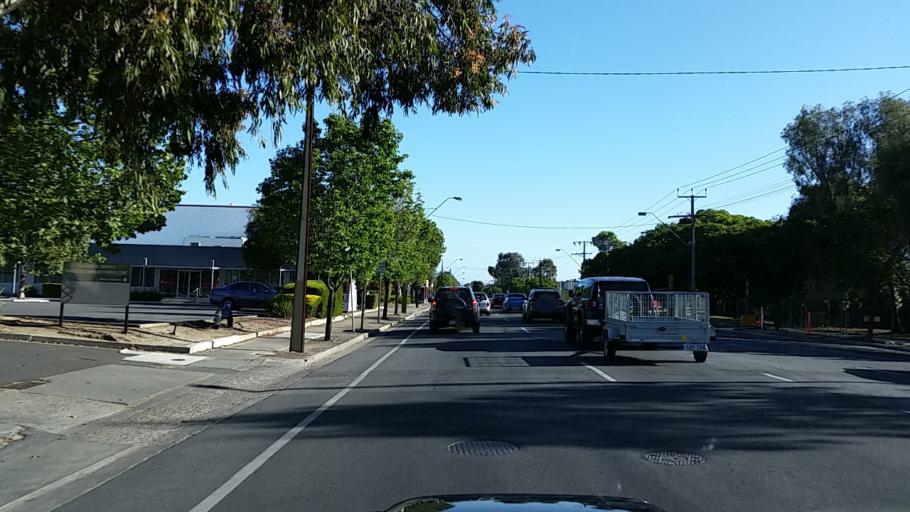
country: AU
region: South Australia
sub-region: City of West Torrens
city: Plympton
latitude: -34.9445
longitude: 138.5534
